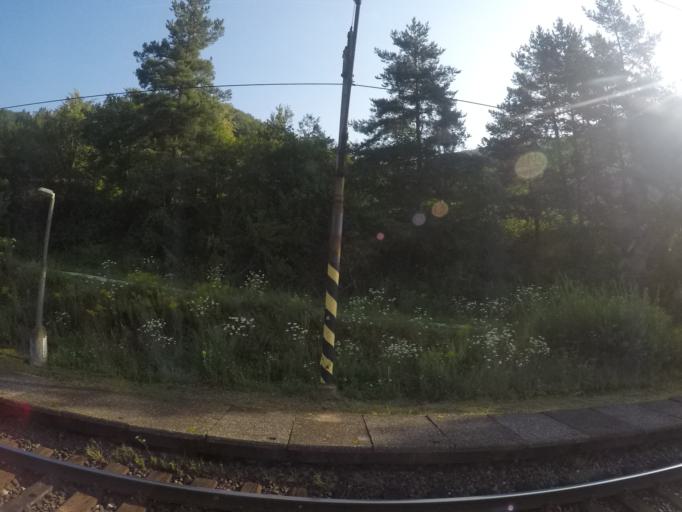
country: SK
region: Kosicky
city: Gelnica
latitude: 48.8891
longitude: 21.0425
